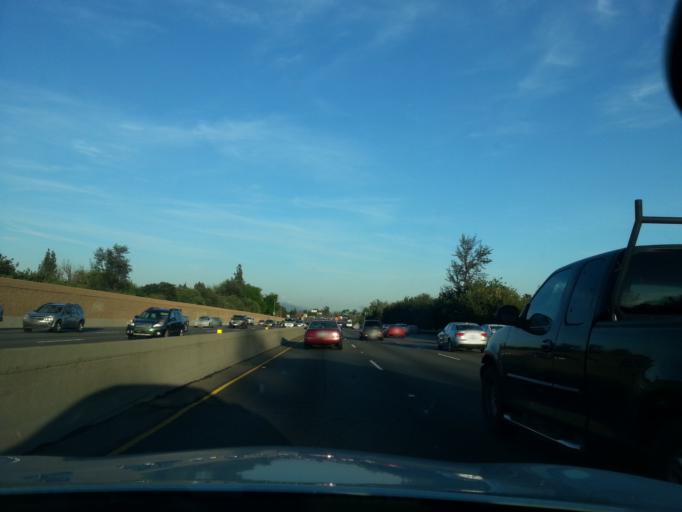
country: US
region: California
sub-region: Los Angeles County
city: Northridge
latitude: 34.1734
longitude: -118.5434
